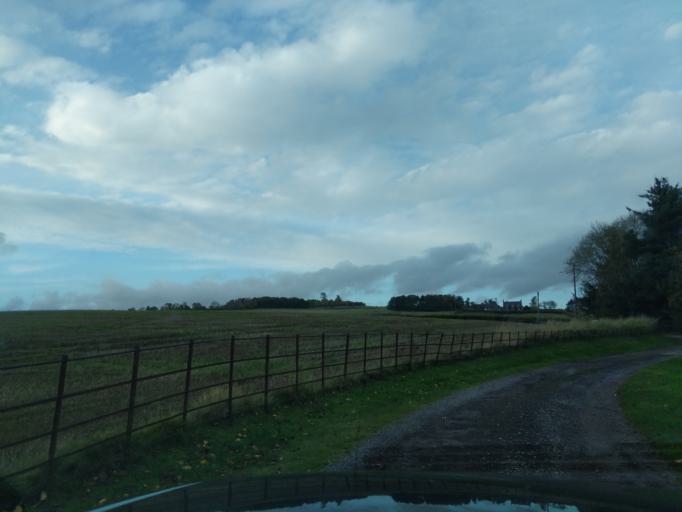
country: GB
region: Scotland
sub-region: Fife
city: Newport-On-Tay
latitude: 56.4211
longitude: -2.9136
